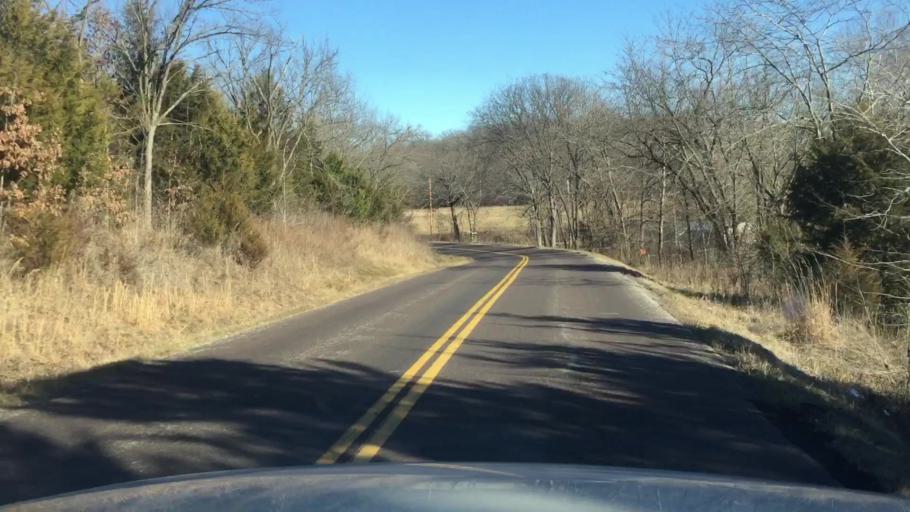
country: US
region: Missouri
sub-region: Miller County
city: Eldon
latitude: 38.3401
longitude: -92.7112
